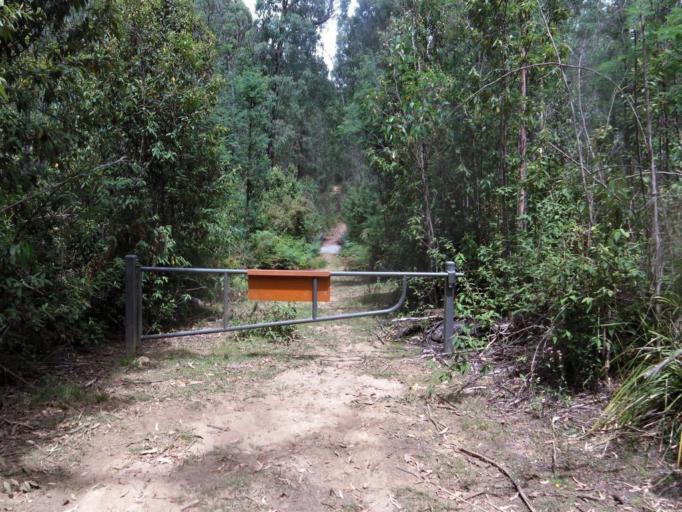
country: AU
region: Victoria
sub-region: Yarra Ranges
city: Healesville
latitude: -37.4504
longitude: 145.5856
